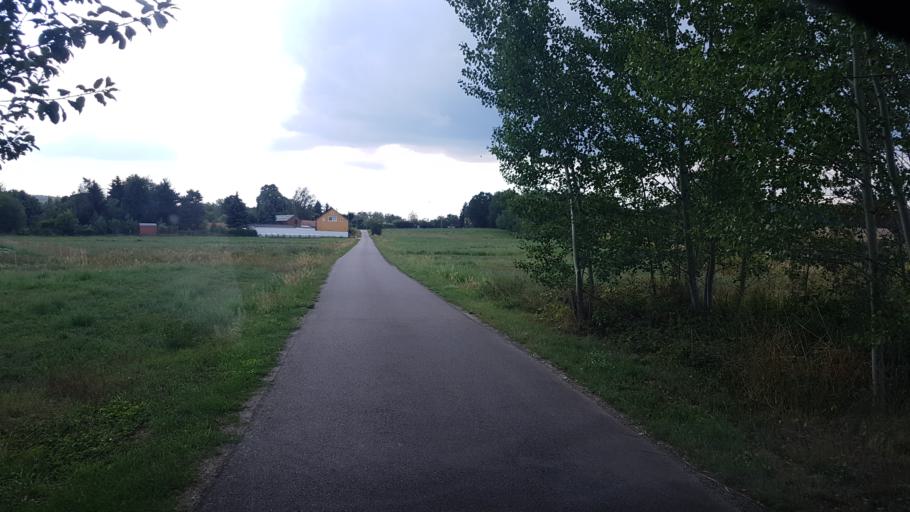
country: DE
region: Brandenburg
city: Calau
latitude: 51.7274
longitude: 13.9534
